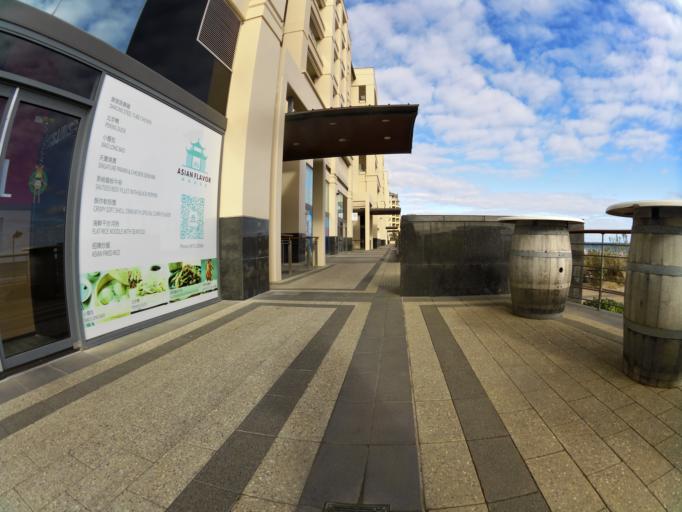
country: AU
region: South Australia
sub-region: Adelaide
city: Glenelg
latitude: -34.9758
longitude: 138.5099
